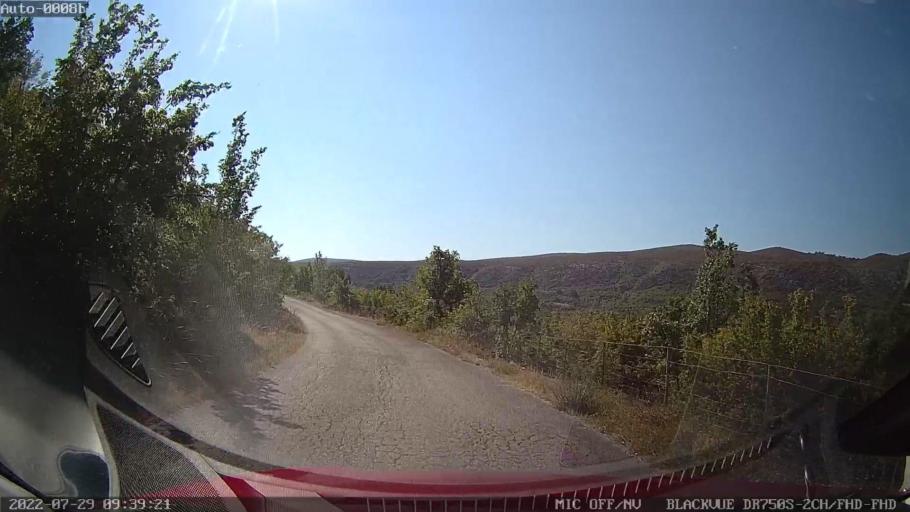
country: HR
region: Zadarska
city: Obrovac
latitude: 44.1947
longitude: 15.7551
